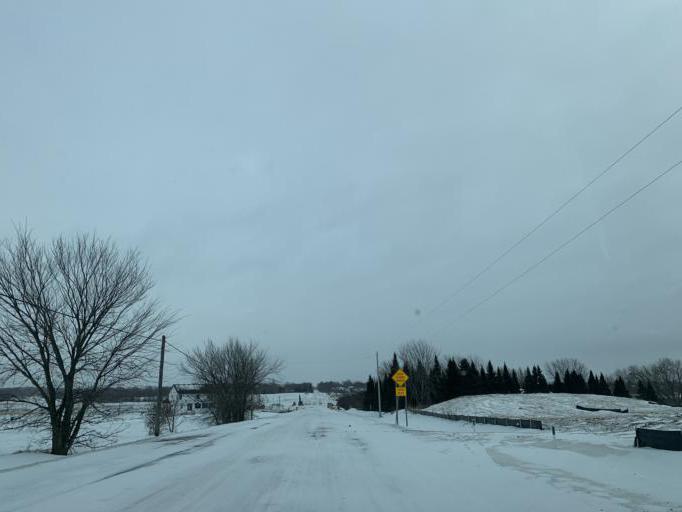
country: US
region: Minnesota
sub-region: Washington County
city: Cottage Grove
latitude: 44.8578
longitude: -92.9175
